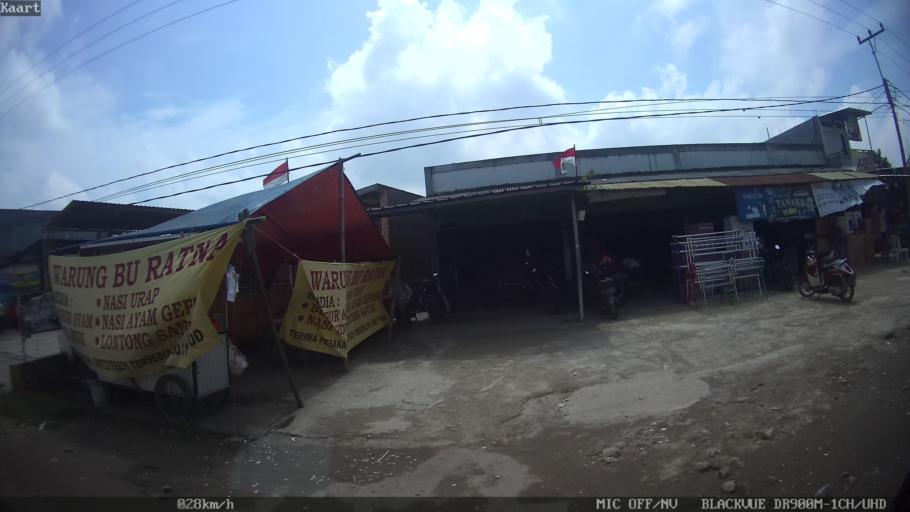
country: ID
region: Lampung
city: Kedaton
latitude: -5.3408
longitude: 105.2940
